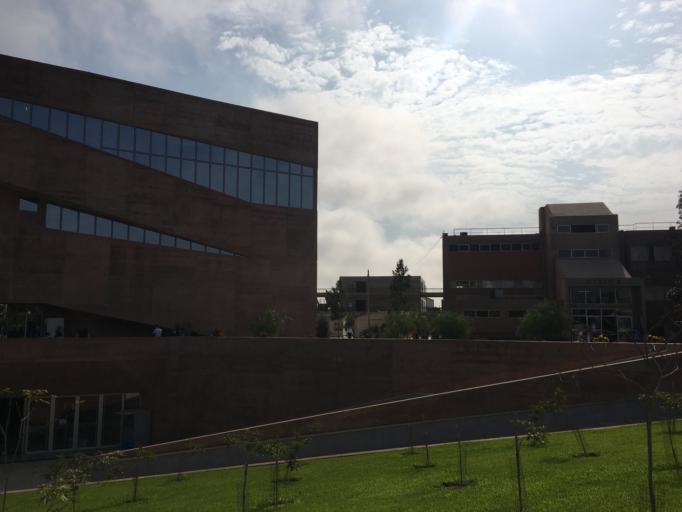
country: PE
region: Callao
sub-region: Callao
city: Callao
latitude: -12.0716
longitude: -77.0799
